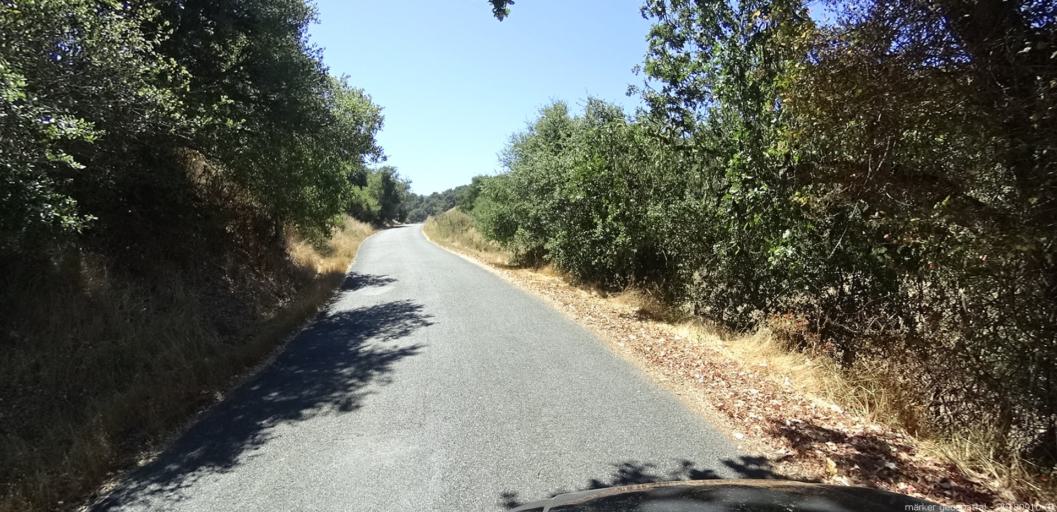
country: US
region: California
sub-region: Monterey County
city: Carmel Valley Village
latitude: 36.4735
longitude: -121.8018
